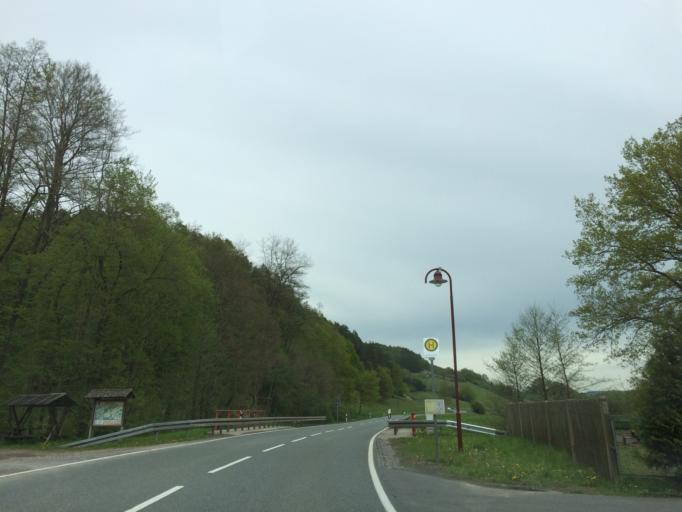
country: DE
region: Thuringia
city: Freienorla
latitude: 50.7507
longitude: 11.5582
